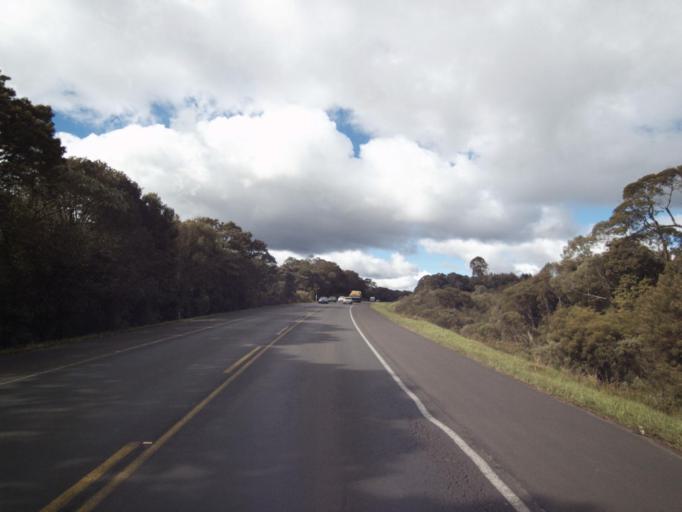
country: BR
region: Santa Catarina
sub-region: Concordia
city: Concordia
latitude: -26.9722
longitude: -51.8361
